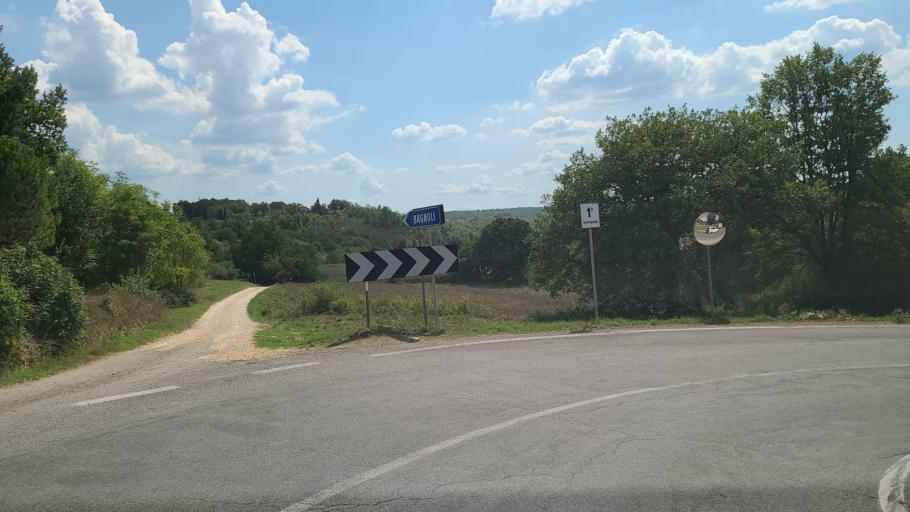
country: IT
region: Tuscany
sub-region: Provincia di Siena
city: Colle di Val d'Elsa
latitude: 43.4121
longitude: 11.0744
